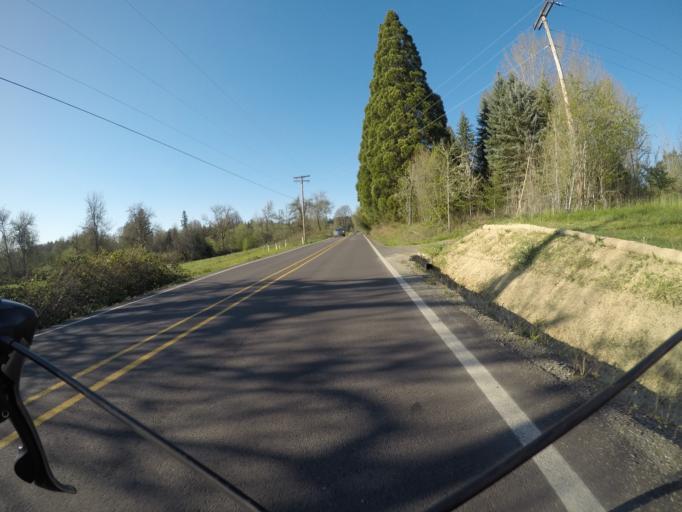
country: US
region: Oregon
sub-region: Washington County
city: Aloha
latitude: 45.4332
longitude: -122.8861
